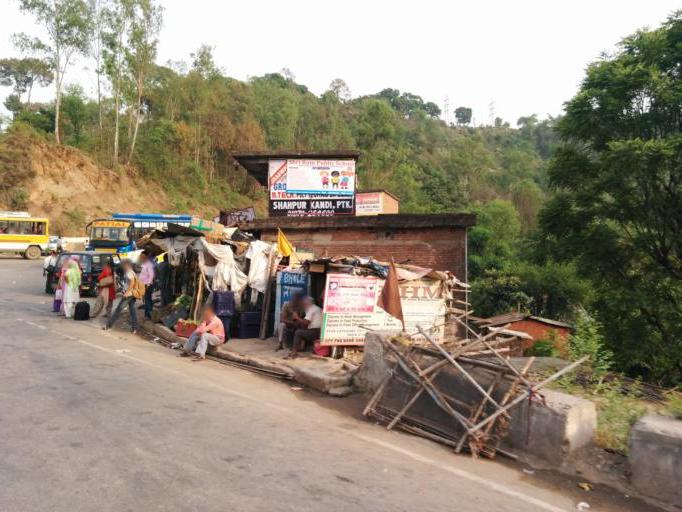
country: IN
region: Himachal Pradesh
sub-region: Kangra
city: Kotla
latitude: 32.2285
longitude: 76.0809
